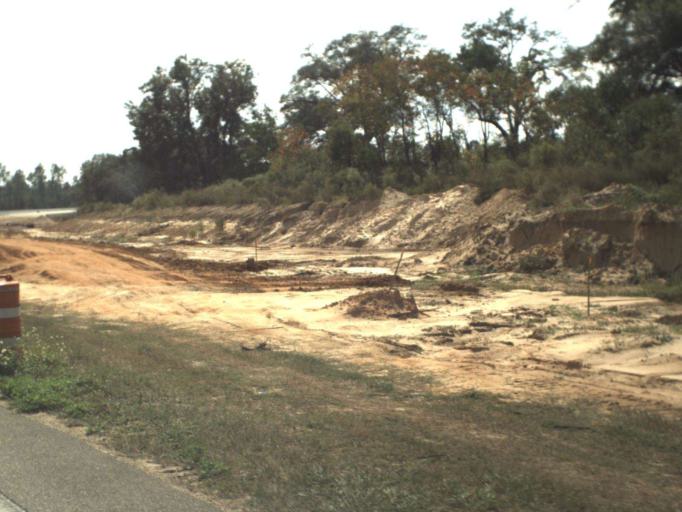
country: US
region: Florida
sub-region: Holmes County
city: Bonifay
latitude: 30.6709
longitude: -85.6868
